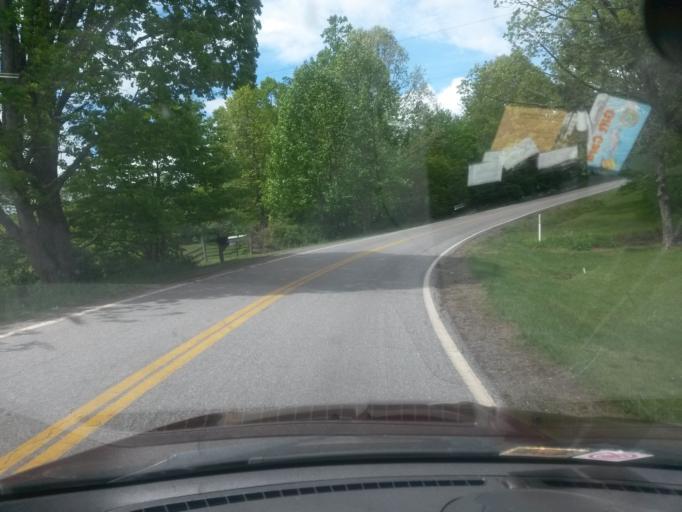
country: US
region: Virginia
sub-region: Floyd County
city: Floyd
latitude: 36.7568
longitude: -80.3919
